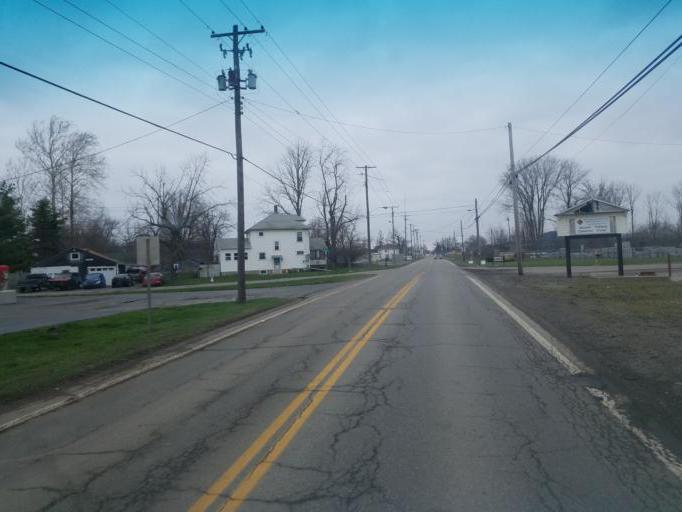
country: US
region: Ohio
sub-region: Marion County
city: Marion
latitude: 40.5657
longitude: -83.1379
